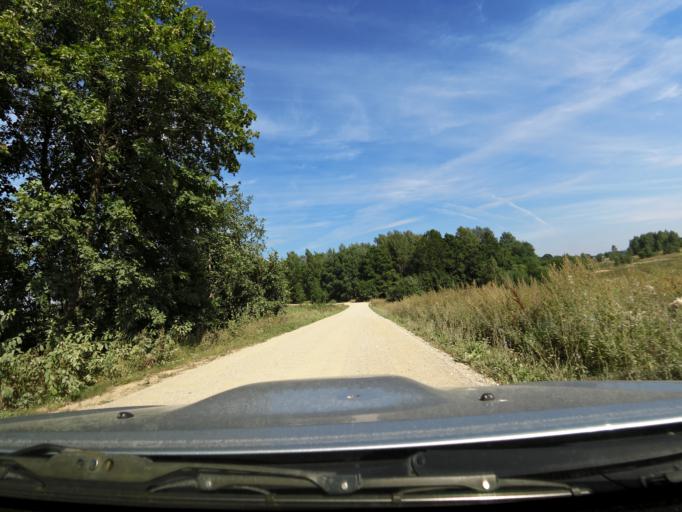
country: LT
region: Vilnius County
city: Pasilaiciai
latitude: 54.8346
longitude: 25.1700
